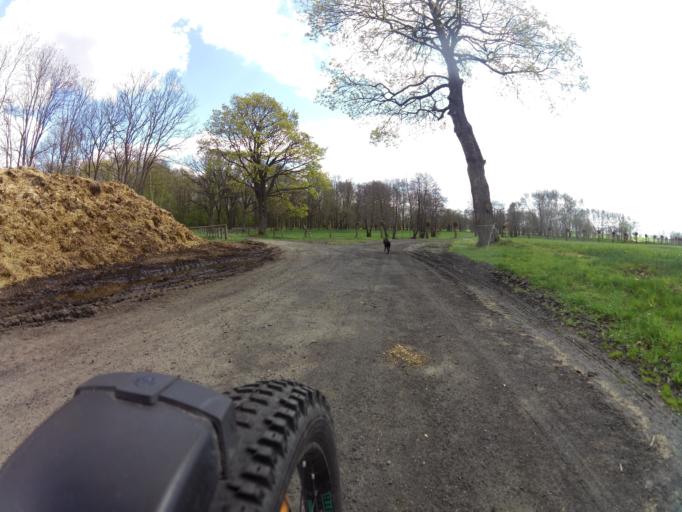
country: PL
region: West Pomeranian Voivodeship
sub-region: Powiat gryficki
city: Gryfice
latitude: 53.8482
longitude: 15.1726
